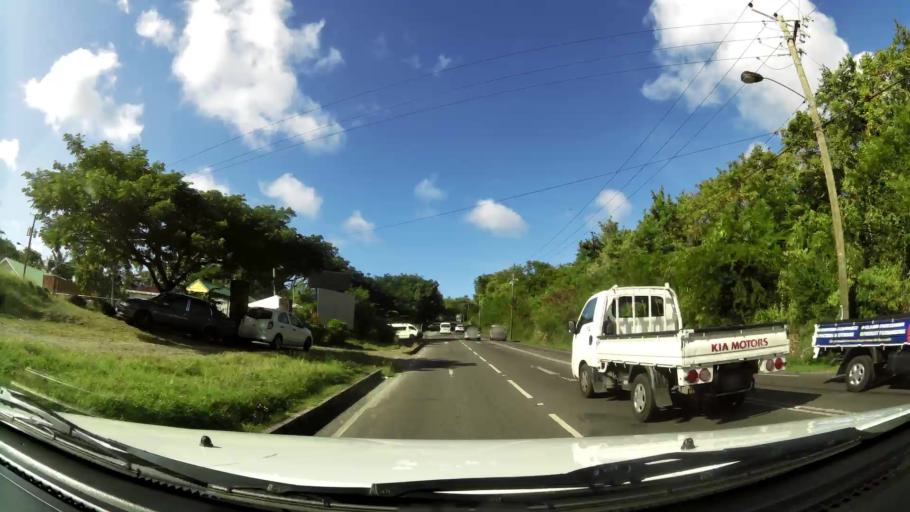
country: LC
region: Castries Quarter
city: Bisee
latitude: 14.0392
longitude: -60.9691
